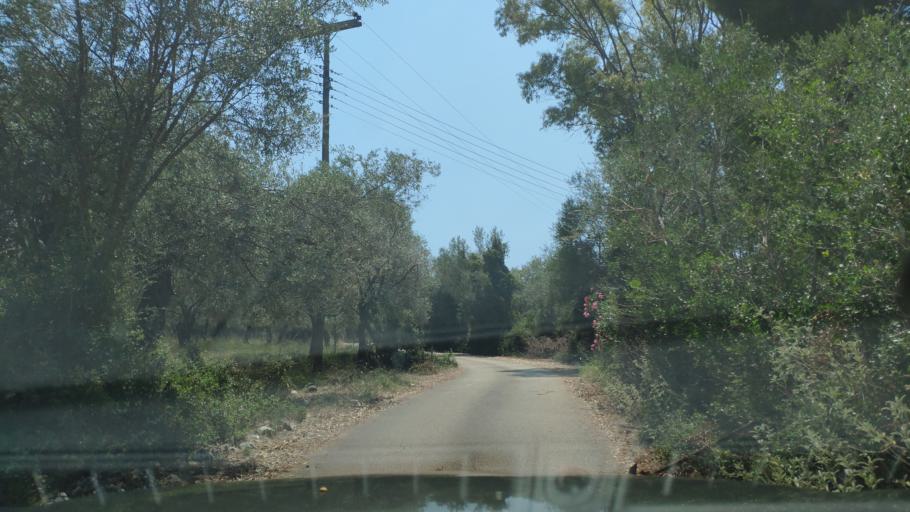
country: GR
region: West Greece
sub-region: Nomos Aitolias kai Akarnanias
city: Amfilochia
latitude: 38.9030
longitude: 21.1177
